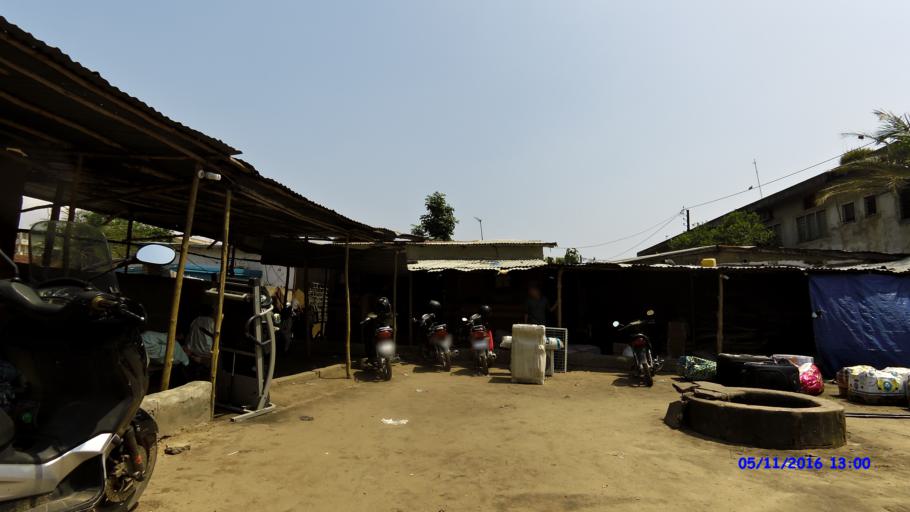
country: BJ
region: Littoral
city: Cotonou
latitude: 6.3576
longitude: 2.4224
